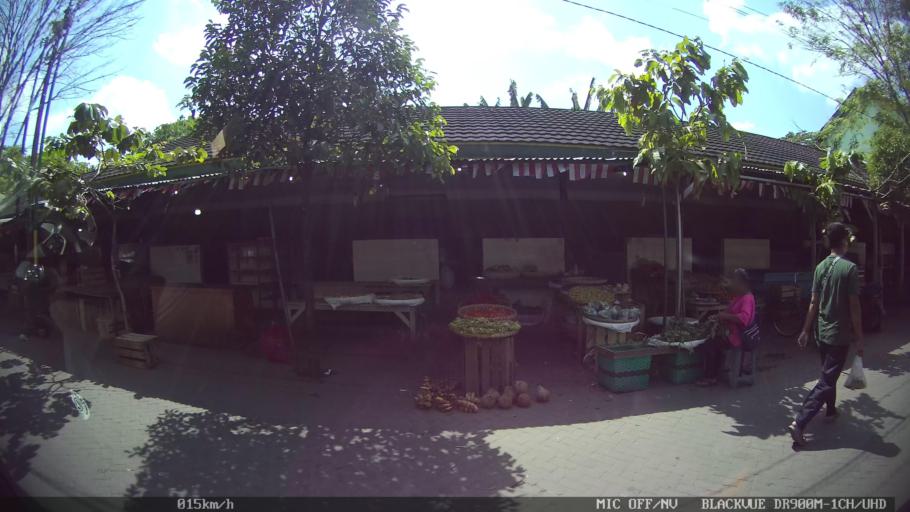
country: ID
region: Daerah Istimewa Yogyakarta
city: Sewon
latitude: -7.8331
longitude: 110.3883
